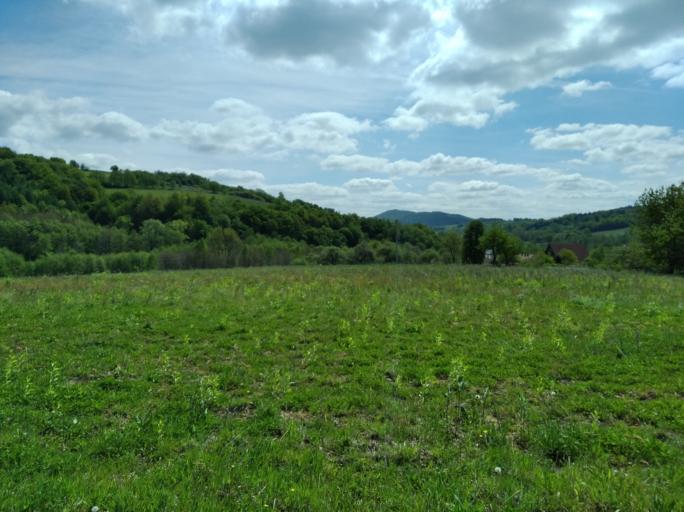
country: PL
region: Subcarpathian Voivodeship
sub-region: Powiat strzyzowski
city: Frysztak
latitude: 49.8744
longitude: 21.5946
